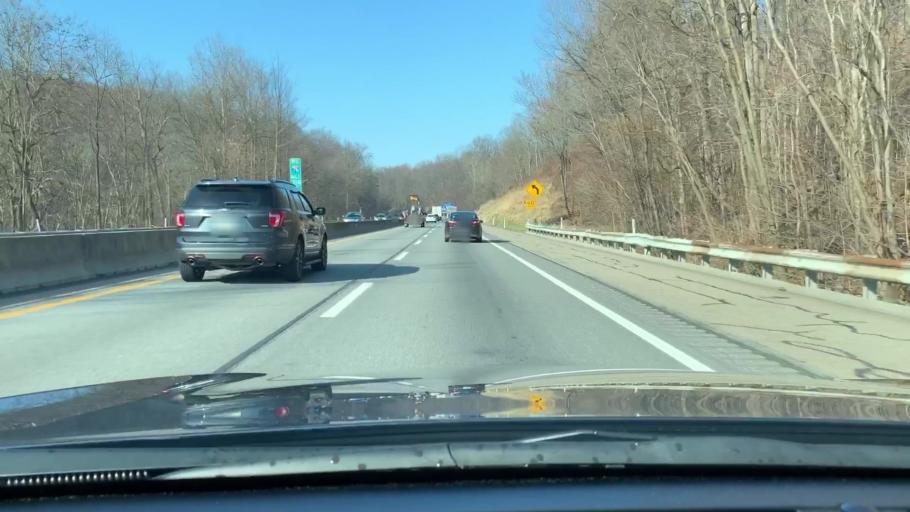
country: US
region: Pennsylvania
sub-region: Chester County
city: Downingtown
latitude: 40.0935
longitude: -75.7326
